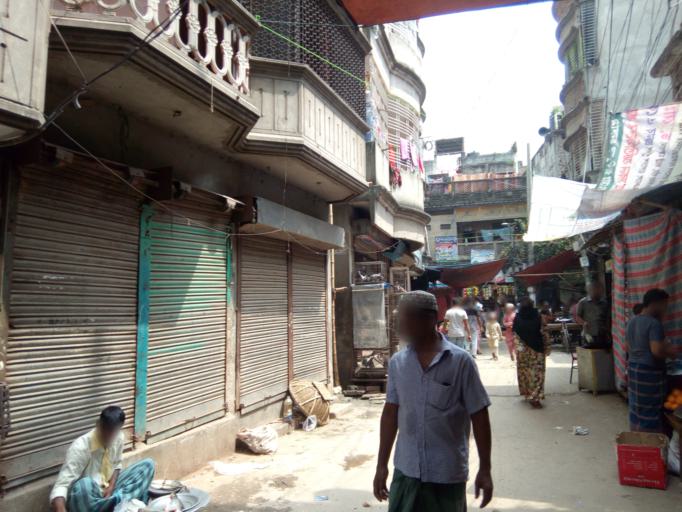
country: BD
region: Dhaka
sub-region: Dhaka
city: Dhaka
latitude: 23.7165
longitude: 90.4052
